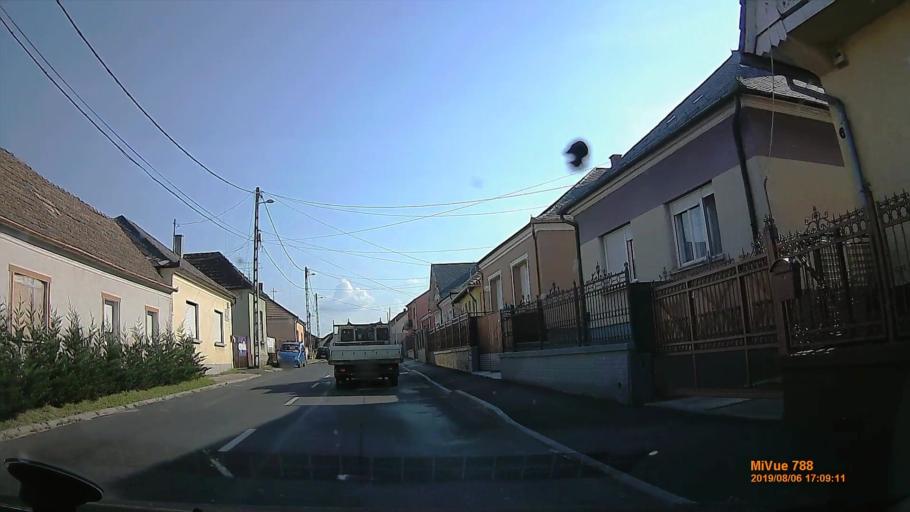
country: HU
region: Zala
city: Nagykanizsa
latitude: 46.4545
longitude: 16.9569
